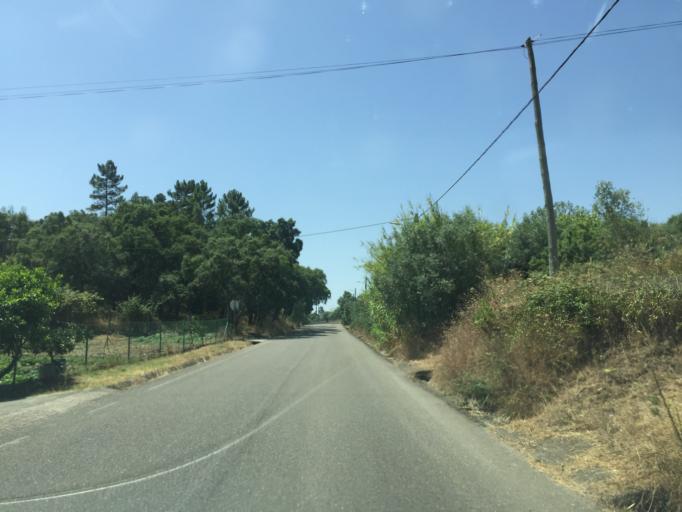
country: PT
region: Santarem
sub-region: Ferreira do Zezere
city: Ferreira do Zezere
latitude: 39.6343
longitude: -8.3073
